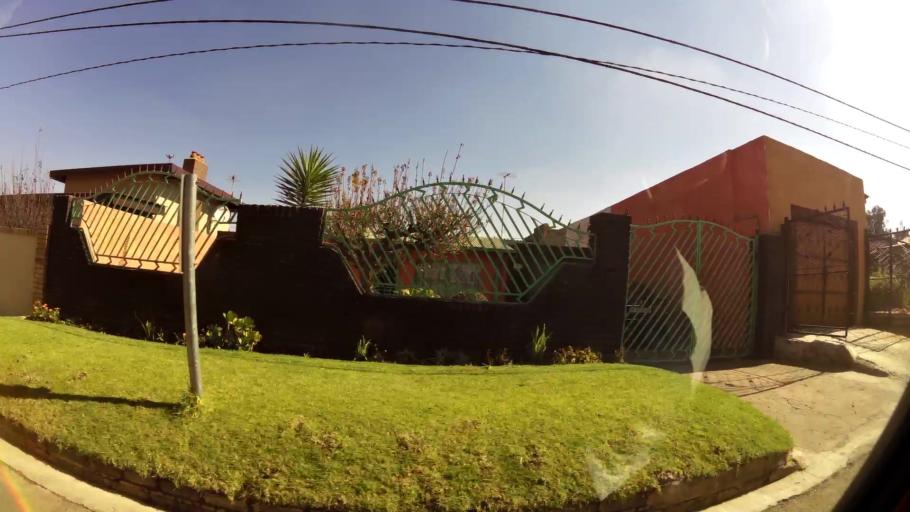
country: ZA
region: Gauteng
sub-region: City of Johannesburg Metropolitan Municipality
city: Soweto
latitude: -26.2386
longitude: 27.8997
